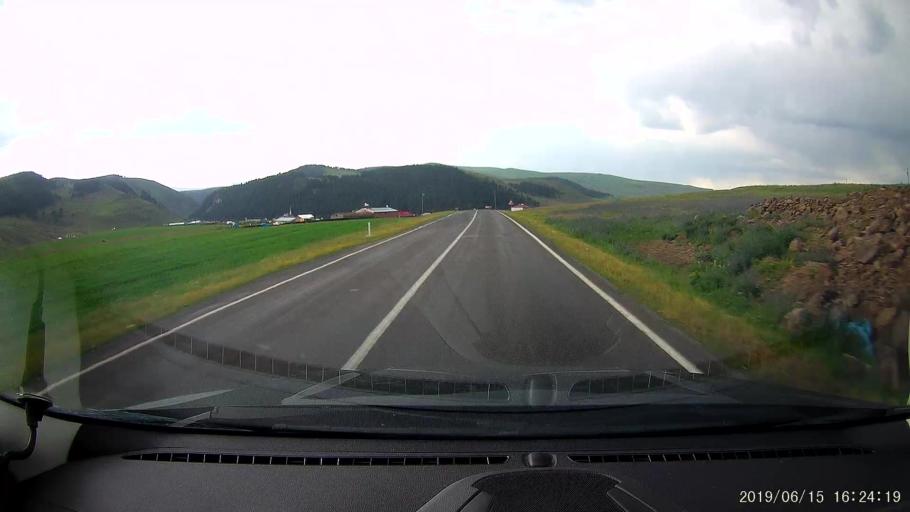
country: TR
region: Ardahan
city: Hanak
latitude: 41.1661
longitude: 42.8697
